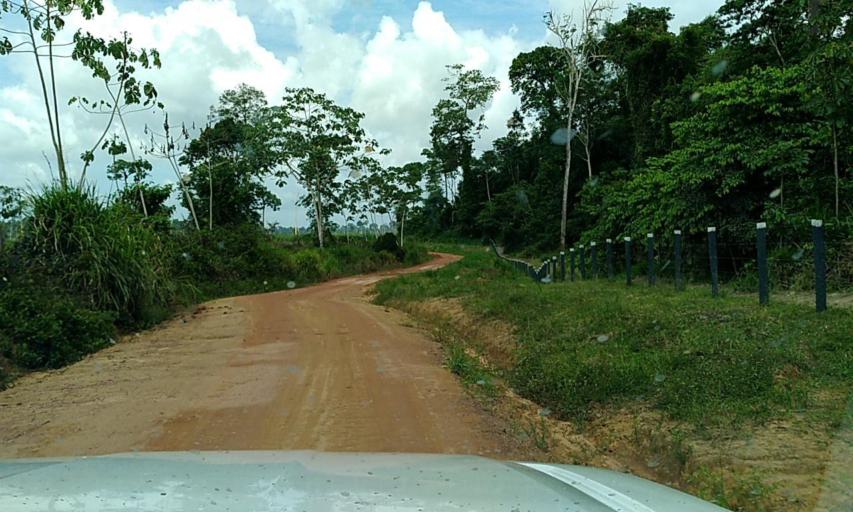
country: BR
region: Para
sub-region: Senador Jose Porfirio
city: Senador Jose Porfirio
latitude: -2.5218
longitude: -51.8514
